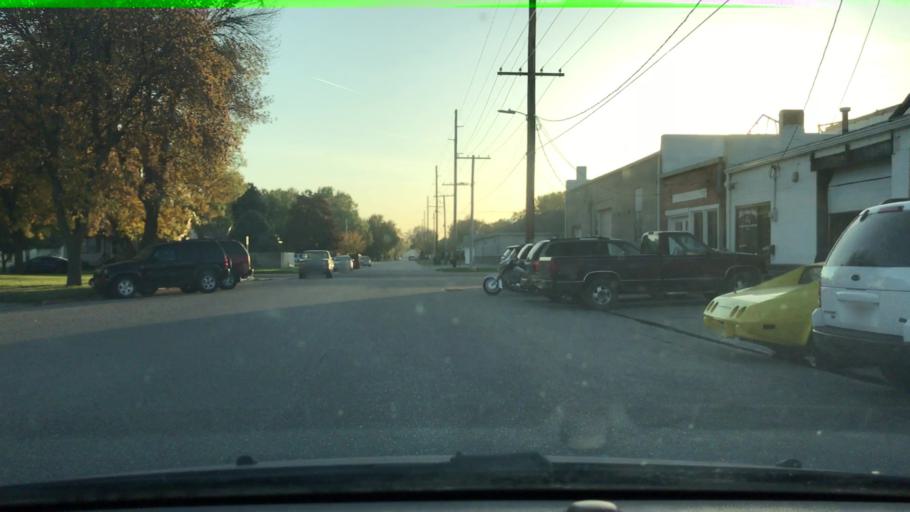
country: US
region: Nebraska
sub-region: Merrick County
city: Central City
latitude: 41.1144
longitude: -98.0029
